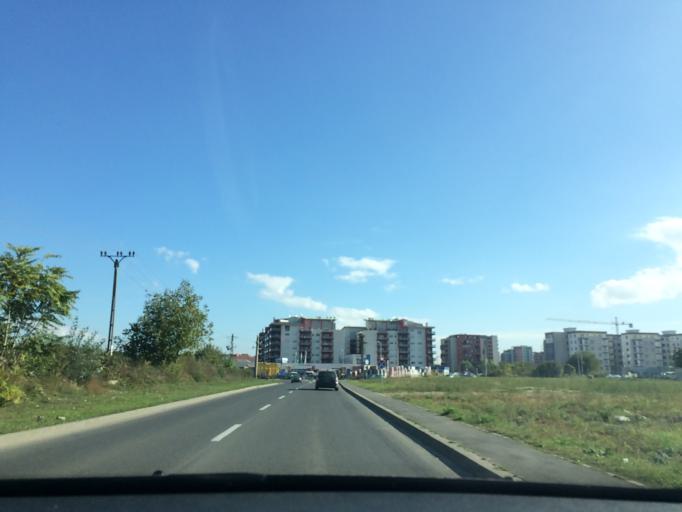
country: RO
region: Timis
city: Timisoara
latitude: 45.7775
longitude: 21.2084
